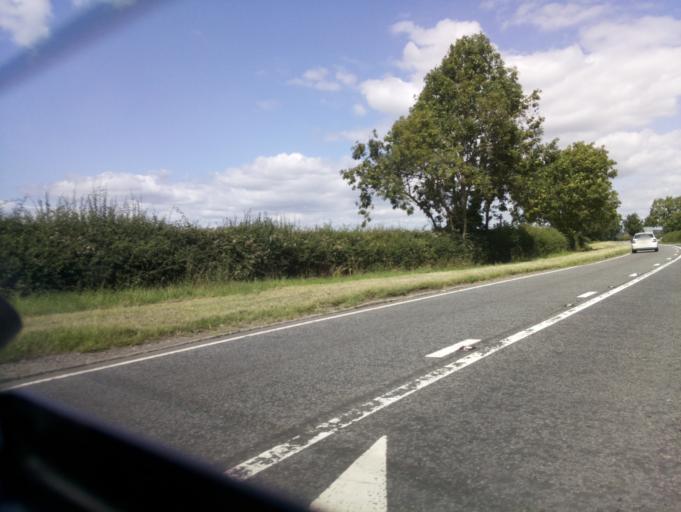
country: GB
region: England
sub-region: Buckinghamshire
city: Aylesbury
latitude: 51.8518
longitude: -0.8284
